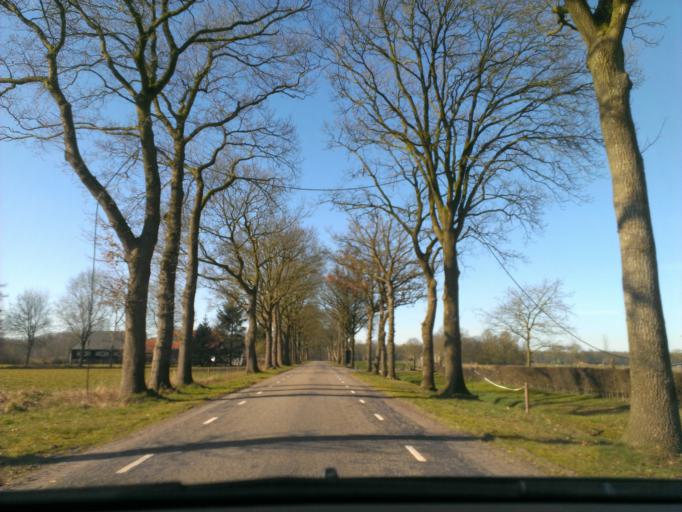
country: NL
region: Drenthe
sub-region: Gemeente Hoogeveen
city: Hoogeveen
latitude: 52.7237
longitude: 6.4201
